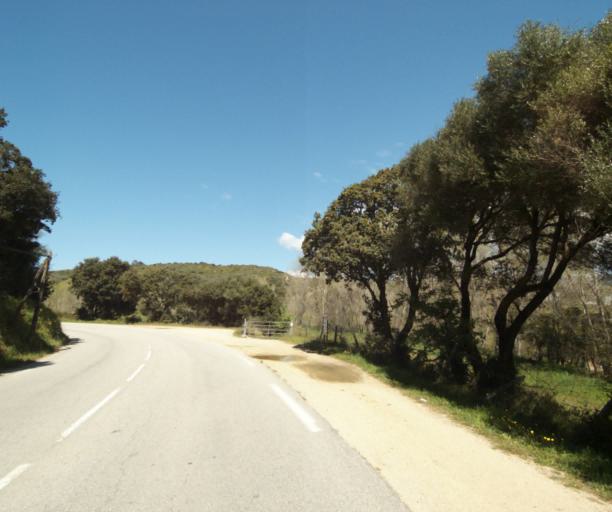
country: FR
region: Corsica
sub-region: Departement de la Corse-du-Sud
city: Propriano
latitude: 41.6590
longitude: 8.9146
